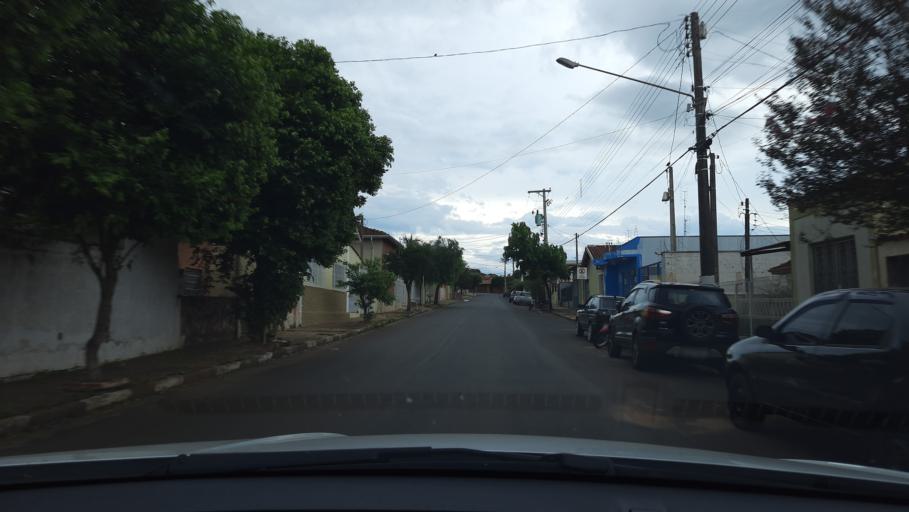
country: BR
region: Sao Paulo
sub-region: Casa Branca
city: Casa Branca
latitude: -21.7796
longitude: -47.0810
